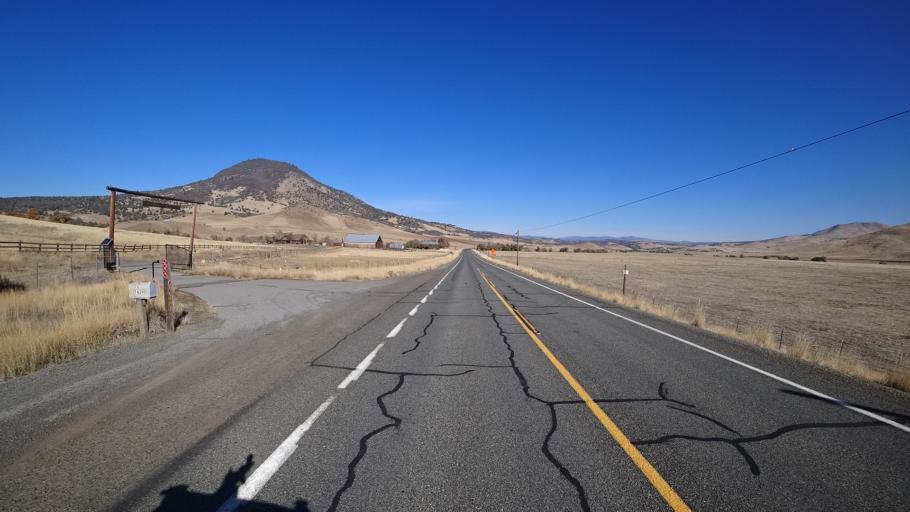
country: US
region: California
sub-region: Siskiyou County
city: Montague
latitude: 41.8231
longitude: -122.4949
